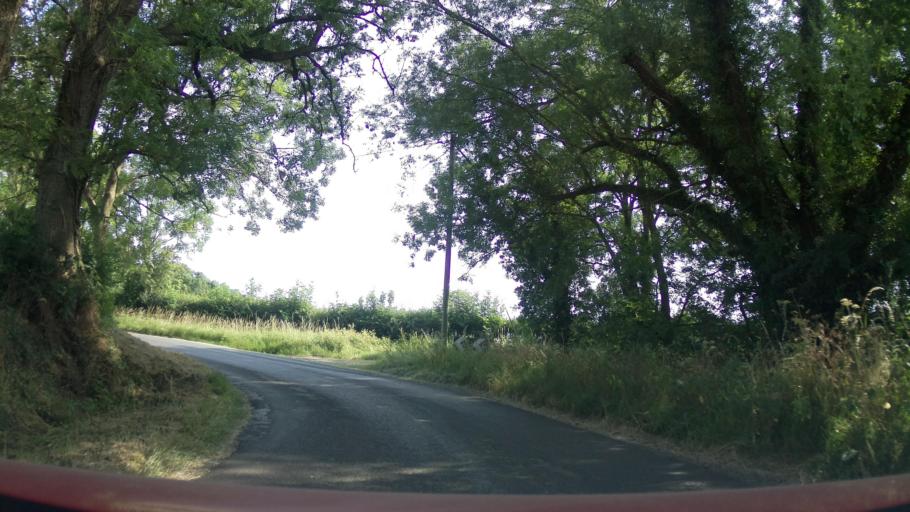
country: GB
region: England
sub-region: Wiltshire
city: Minety
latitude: 51.6341
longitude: -1.9764
